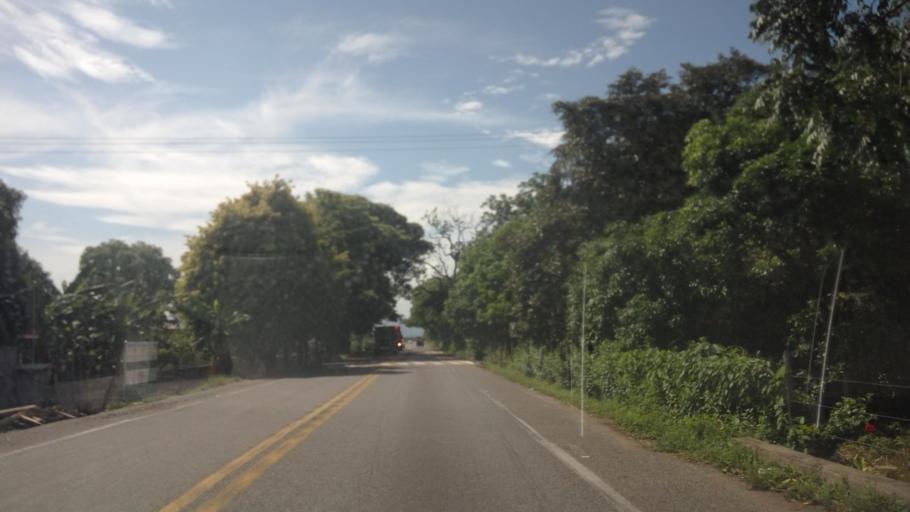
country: MX
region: Tabasco
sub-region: Teapa
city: Eureka y Belen
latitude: 17.6288
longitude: -92.9640
